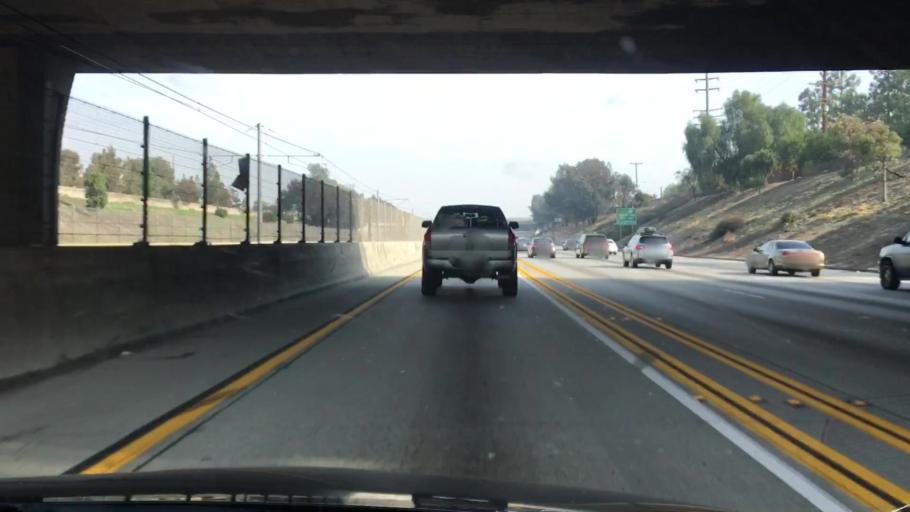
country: US
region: California
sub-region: Los Angeles County
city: Paramount
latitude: 33.9125
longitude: -118.1524
